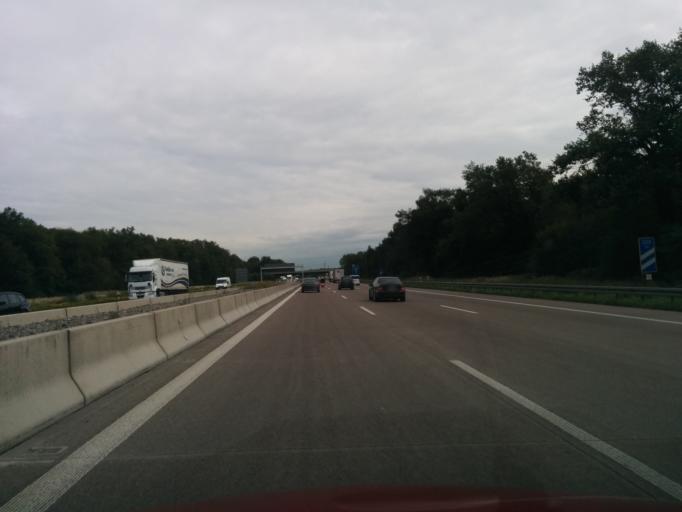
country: DE
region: Baden-Wuerttemberg
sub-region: Karlsruhe Region
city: Forst
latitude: 49.1549
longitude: 8.5645
